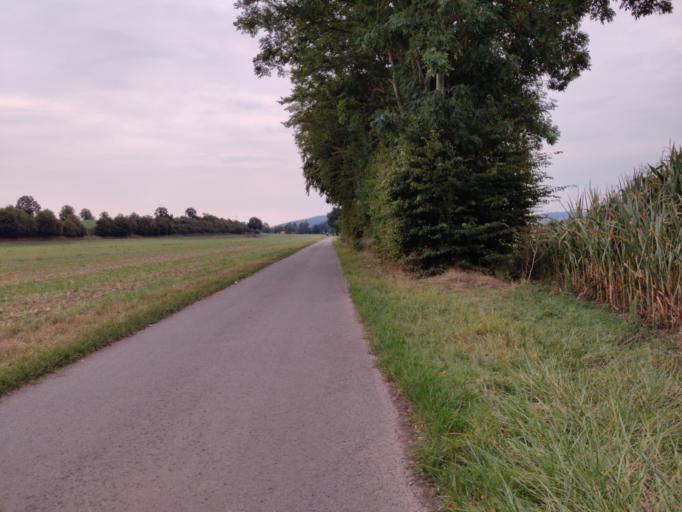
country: DE
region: Lower Saxony
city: Hehlen
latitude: 52.0379
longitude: 9.4191
